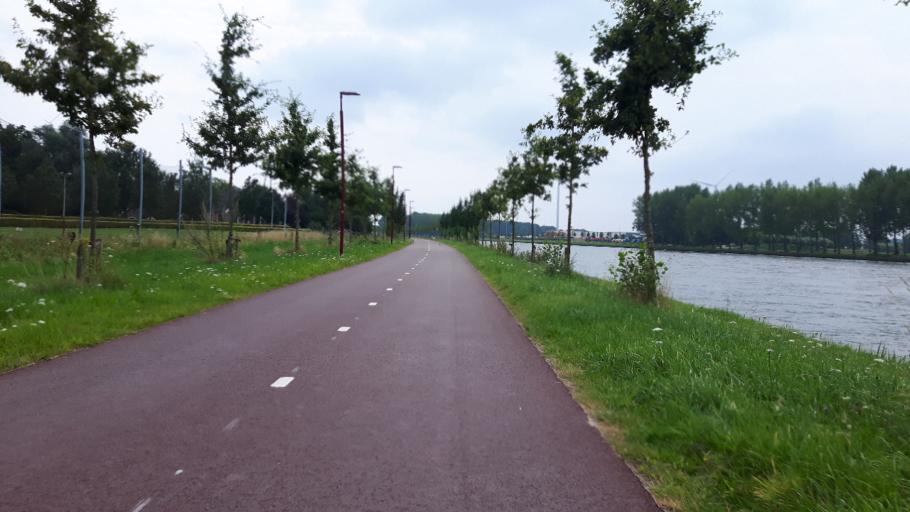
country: NL
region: Utrecht
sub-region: Gemeente Utrecht
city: Lunetten
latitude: 52.0327
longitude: 5.1208
